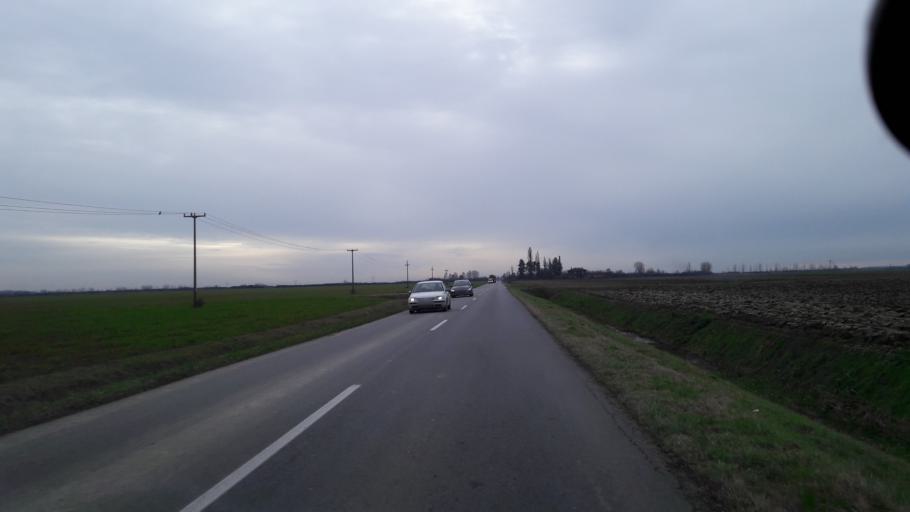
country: HR
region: Osjecko-Baranjska
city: Ovcara
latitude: 45.4873
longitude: 18.5509
